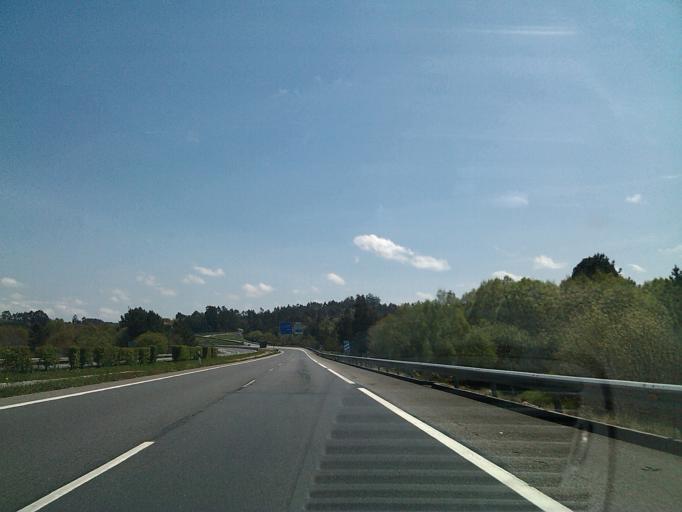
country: ES
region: Galicia
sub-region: Provincia da Coruna
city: Oroso
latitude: 42.9097
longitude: -8.4397
